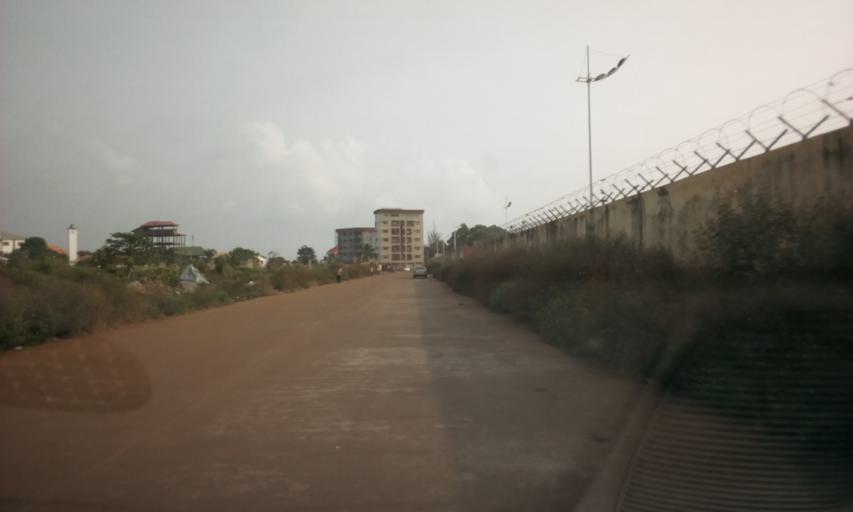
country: GN
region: Conakry
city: Conakry
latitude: 9.6257
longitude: -13.6282
